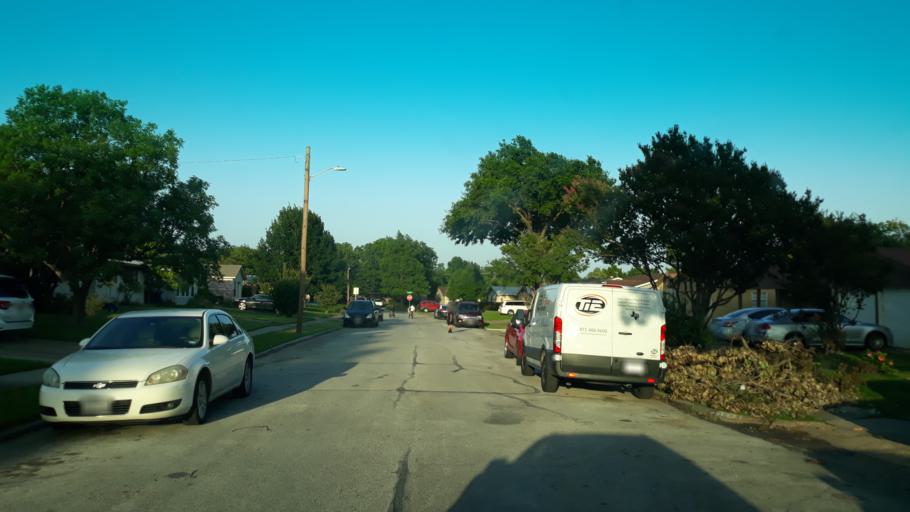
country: US
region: Texas
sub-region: Dallas County
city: Irving
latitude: 32.8518
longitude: -97.0018
